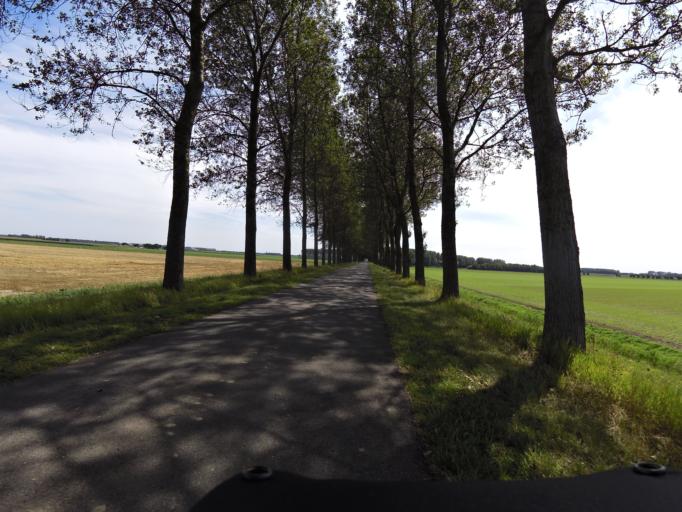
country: NL
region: South Holland
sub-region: Gemeente Goeree-Overflakkee
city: Dirksland
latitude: 51.7953
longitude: 4.0586
